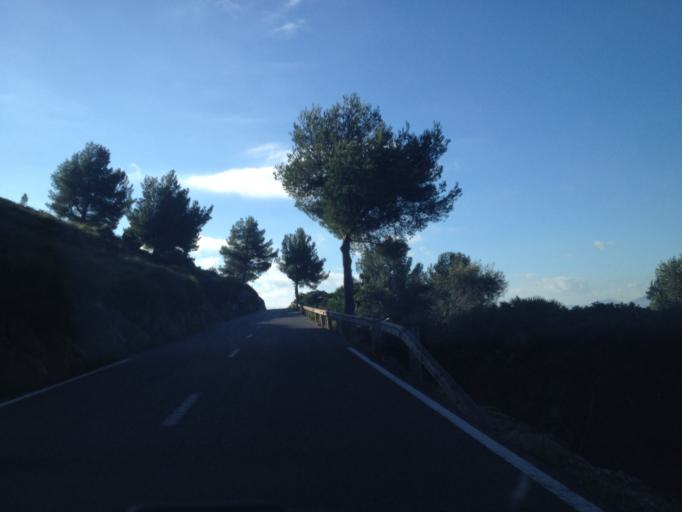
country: ES
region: Balearic Islands
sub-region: Illes Balears
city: Alcudia
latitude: 39.9145
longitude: 3.1046
